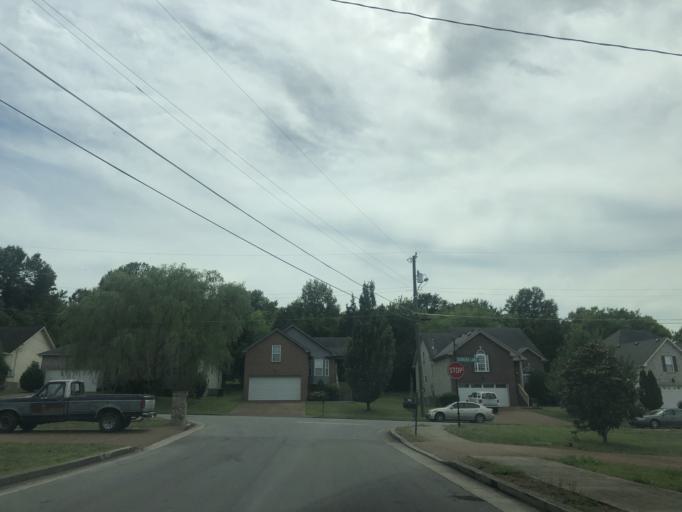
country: US
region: Tennessee
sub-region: Davidson County
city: Nashville
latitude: 36.2114
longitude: -86.8122
